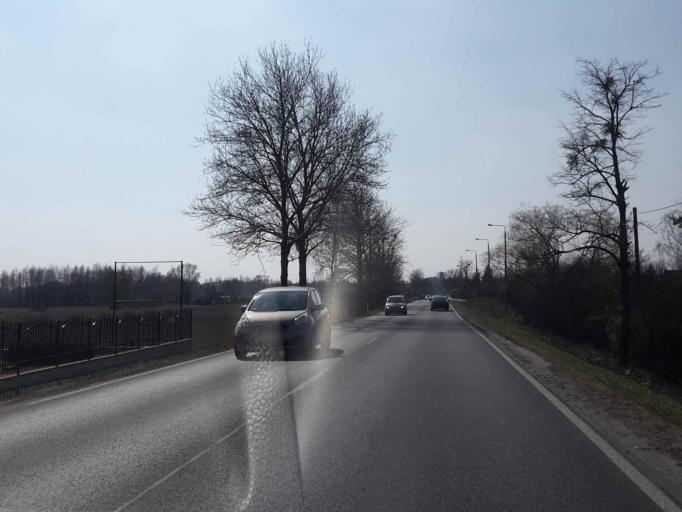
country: PL
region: Kujawsko-Pomorskie
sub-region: Powiat torunski
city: Lubicz Dolny
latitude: 53.0622
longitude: 18.7319
